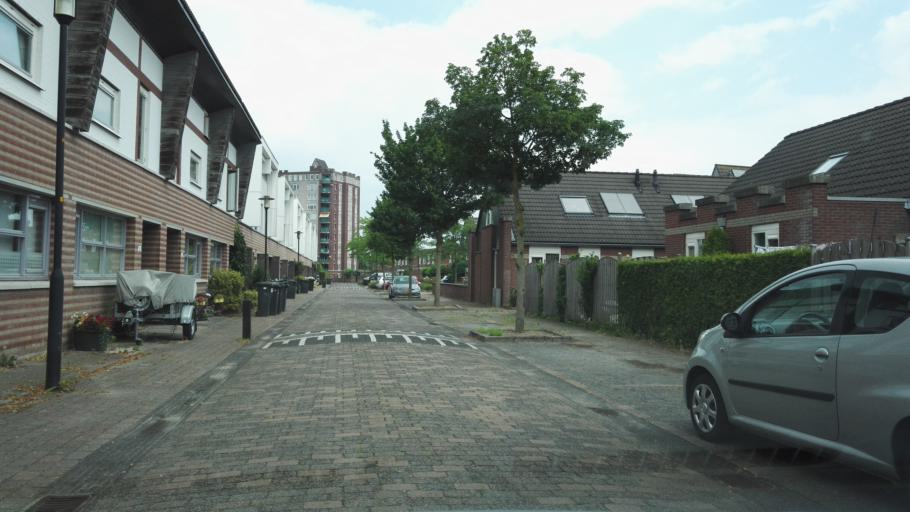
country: NL
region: Gelderland
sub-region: Gemeente Apeldoorn
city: Apeldoorn
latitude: 52.2136
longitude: 6.0139
